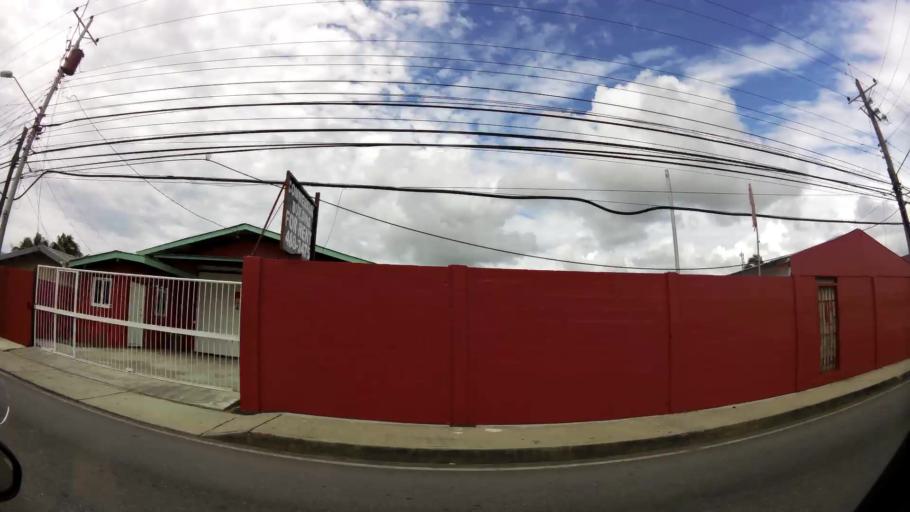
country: TT
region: Chaguanas
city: Chaguanas
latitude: 10.5045
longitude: -61.4076
